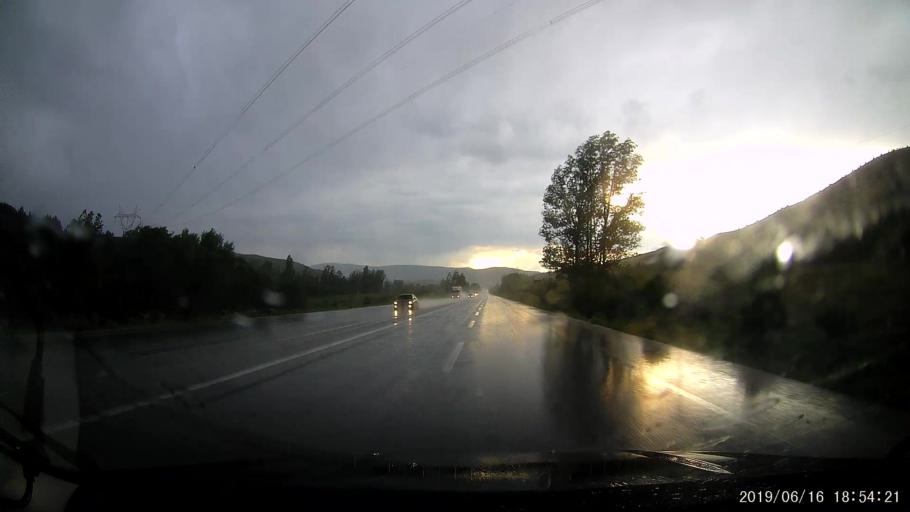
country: TR
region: Erzincan
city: Catalcam
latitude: 39.8967
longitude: 38.8558
